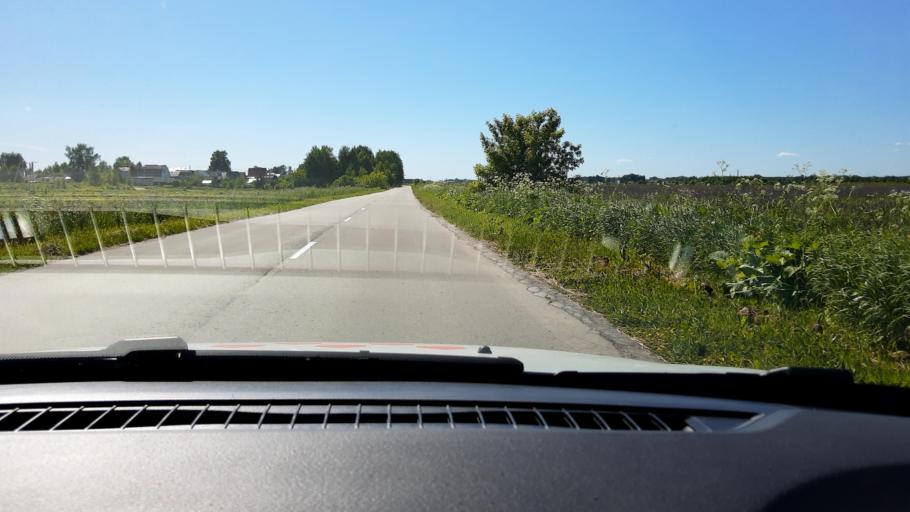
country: RU
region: Nizjnij Novgorod
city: Bor
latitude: 56.3954
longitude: 44.0700
